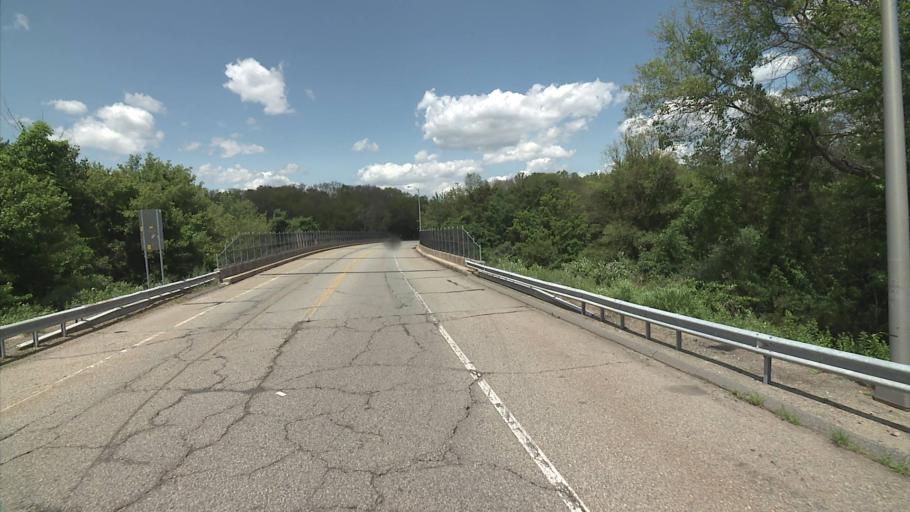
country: US
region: Connecticut
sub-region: New London County
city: Mystic
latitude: 41.3709
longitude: -71.9817
